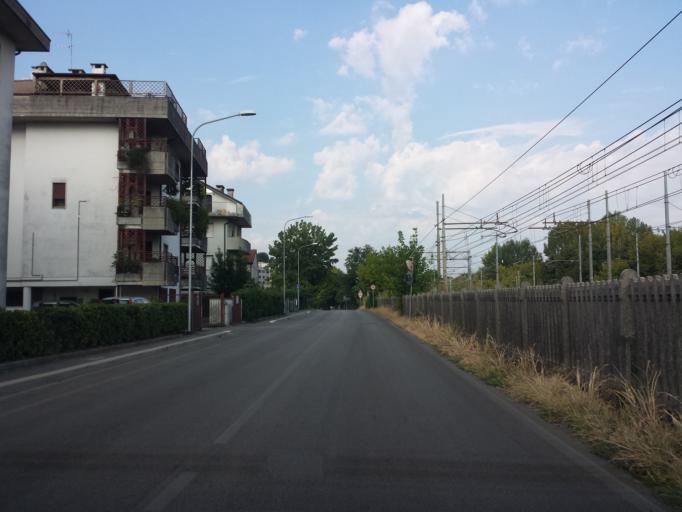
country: IT
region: Veneto
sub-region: Provincia di Vicenza
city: Vicenza
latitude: 45.5421
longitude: 11.5616
